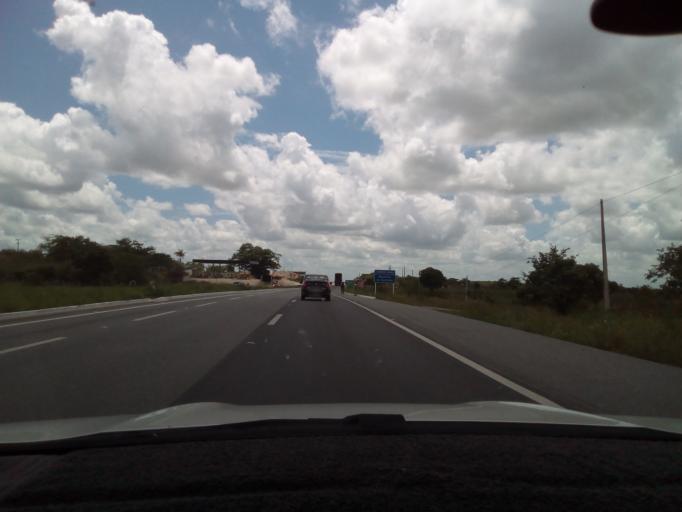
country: BR
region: Paraiba
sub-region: Gurinhem
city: Gurinhem
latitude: -7.1739
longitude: -35.3971
